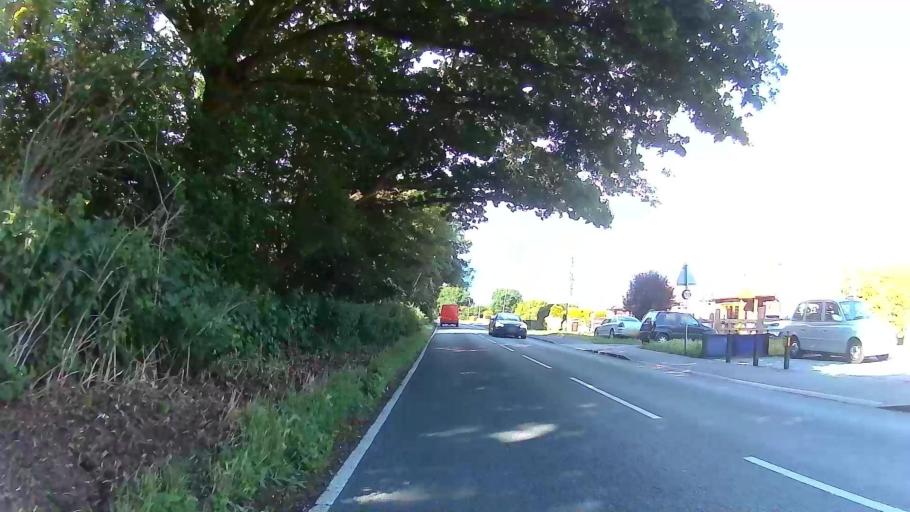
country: GB
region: England
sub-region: Essex
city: Kelvedon Hatch
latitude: 51.6648
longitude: 0.2795
